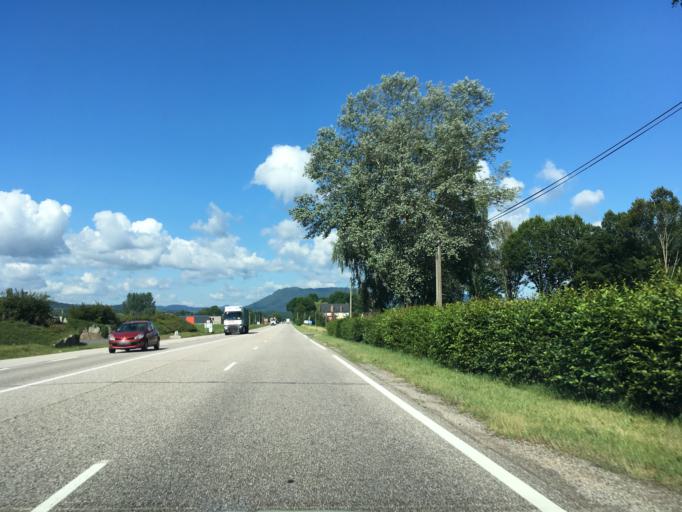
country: FR
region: Lorraine
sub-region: Departement des Vosges
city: Ban-de-Laveline
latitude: 48.2657
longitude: 7.0321
